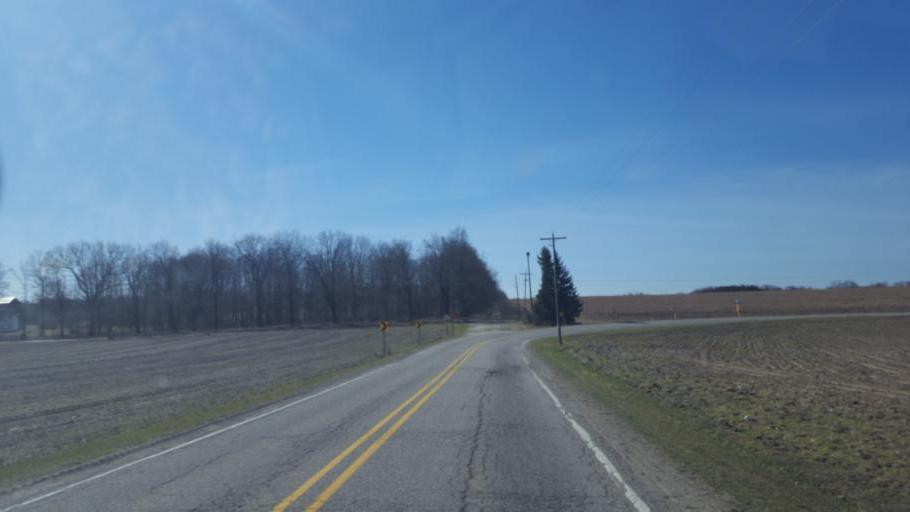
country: US
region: Michigan
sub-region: Montcalm County
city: Edmore
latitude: 43.4891
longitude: -85.0253
